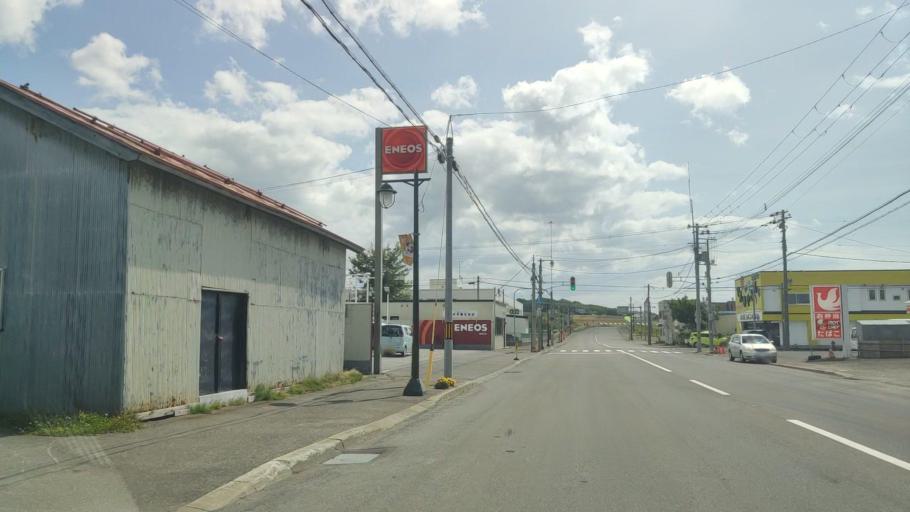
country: JP
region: Hokkaido
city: Makubetsu
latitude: 44.7210
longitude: 141.7929
